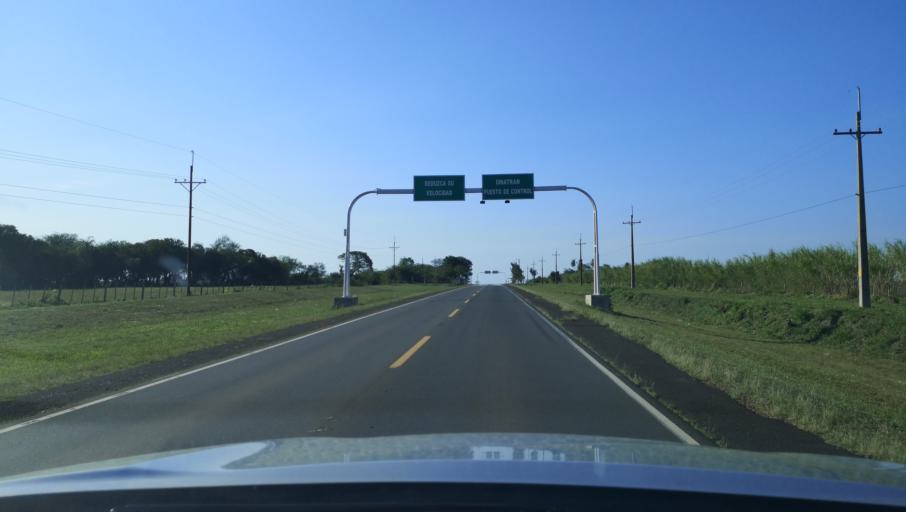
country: PY
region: Misiones
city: Santa Maria
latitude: -26.7853
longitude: -57.0263
